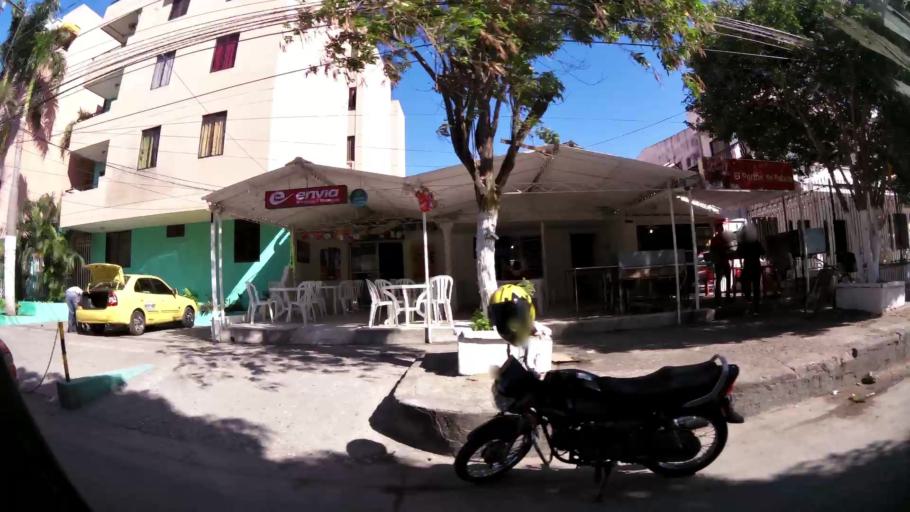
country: CO
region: Atlantico
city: Barranquilla
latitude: 10.9548
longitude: -74.7909
